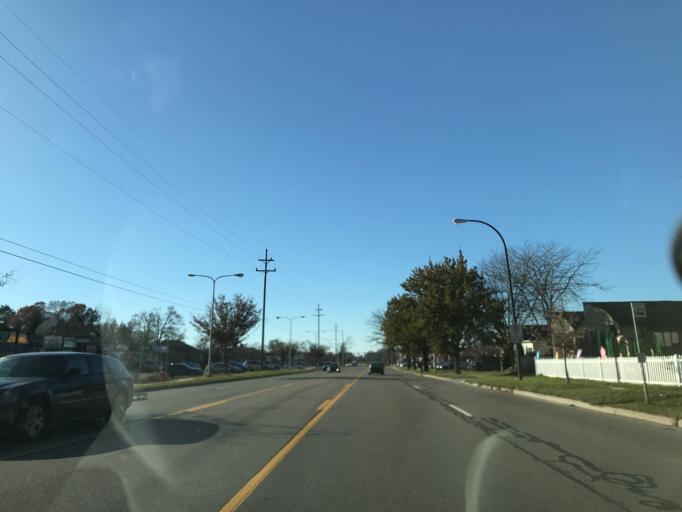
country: US
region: Michigan
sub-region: Washtenaw County
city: Ann Arbor
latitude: 42.2452
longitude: -83.6961
